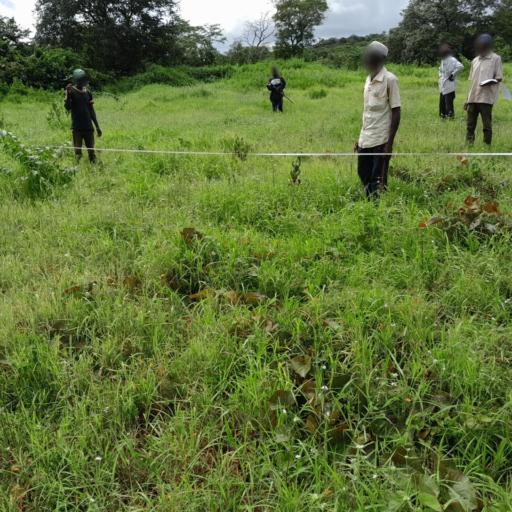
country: GN
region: Boke
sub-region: Boke Prefecture
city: Boke
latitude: 11.0701
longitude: -14.4443
